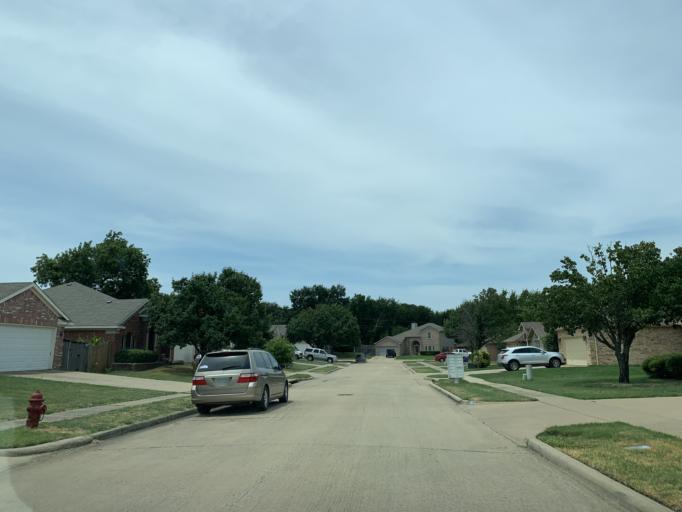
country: US
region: Texas
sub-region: Dallas County
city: Grand Prairie
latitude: 32.6652
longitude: -97.0223
